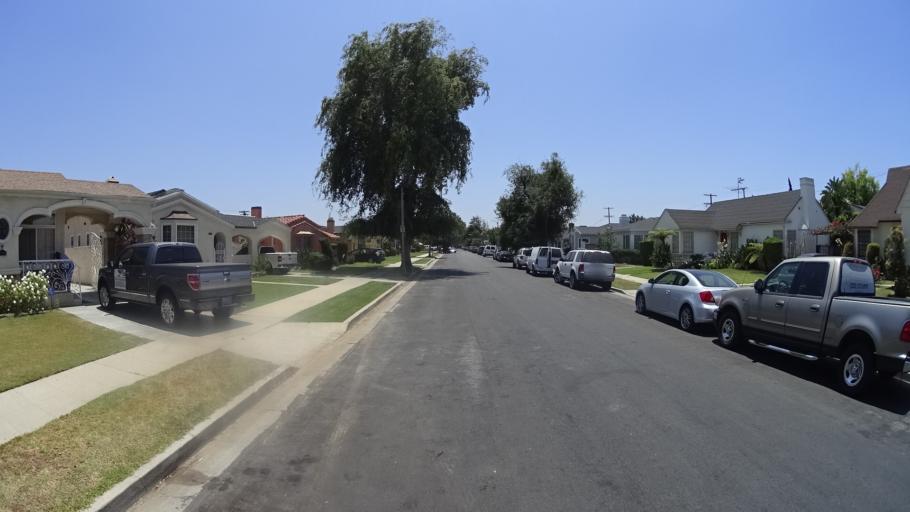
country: US
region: California
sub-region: Los Angeles County
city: View Park-Windsor Hills
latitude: 34.0182
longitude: -118.3224
